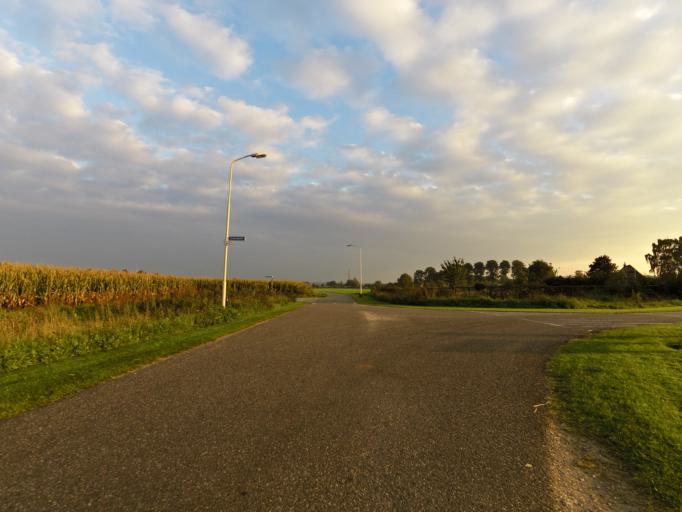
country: NL
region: Gelderland
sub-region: Gemeente Doesburg
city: Doesburg
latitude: 51.9430
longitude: 6.1693
